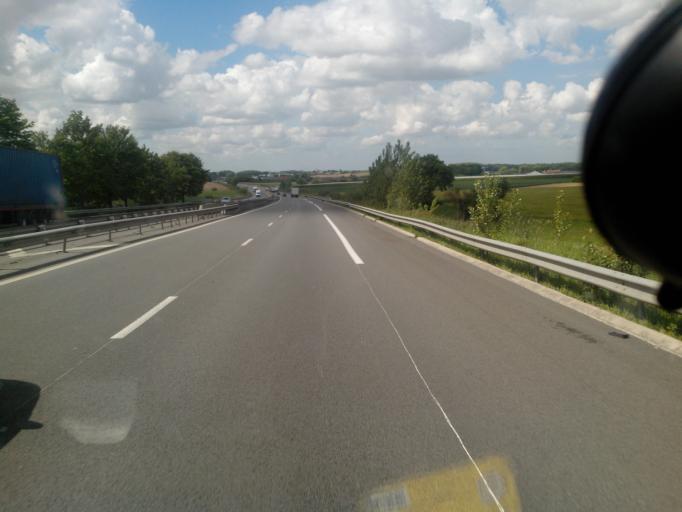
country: FR
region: Nord-Pas-de-Calais
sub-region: Departement du Nord
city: Godewaersvelde
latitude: 50.7872
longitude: 2.6219
